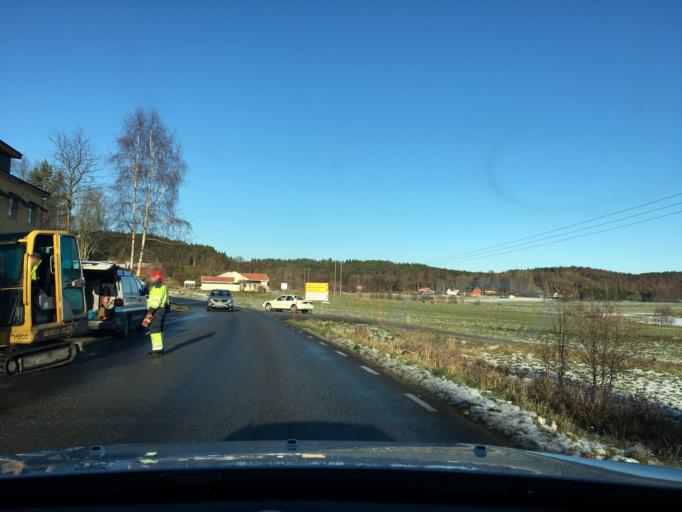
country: SE
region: Vaestra Goetaland
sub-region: Tjorns Kommun
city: Myggenas
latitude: 58.0391
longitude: 11.6743
